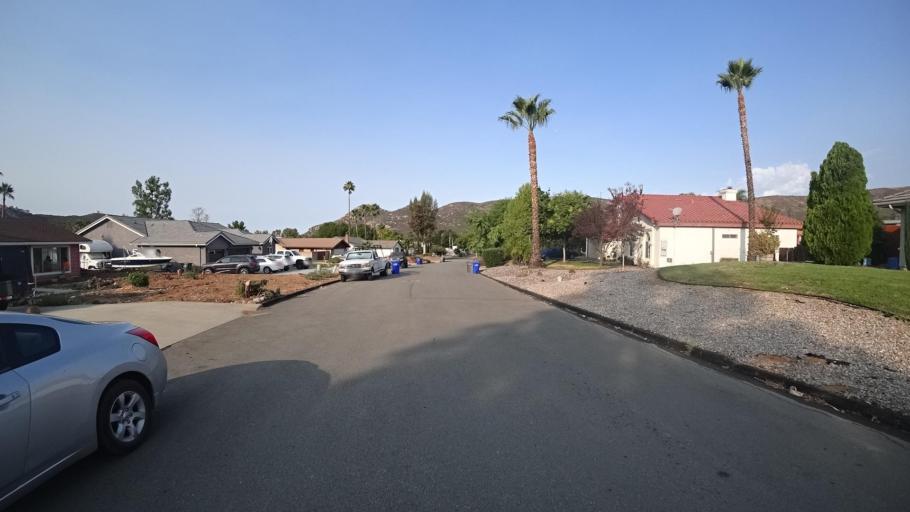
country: US
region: California
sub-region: San Diego County
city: San Diego Country Estates
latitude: 33.0114
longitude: -116.8163
